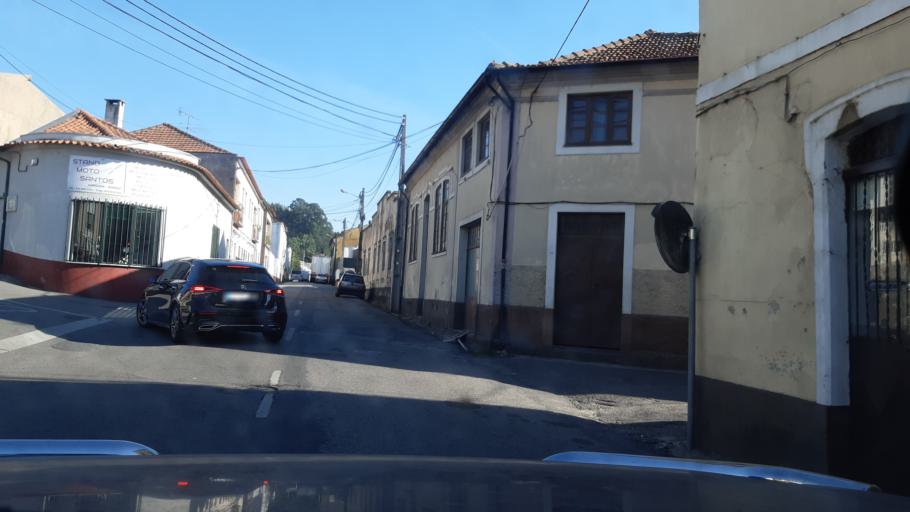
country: PT
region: Aveiro
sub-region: Agueda
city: Agueda
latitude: 40.5720
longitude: -8.4351
